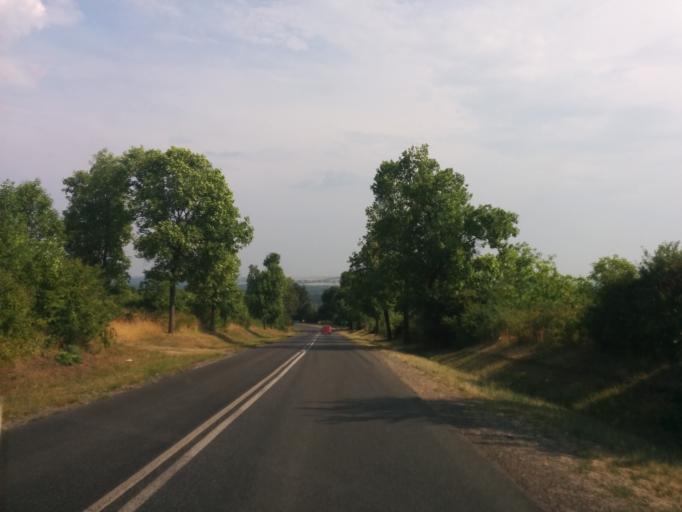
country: PL
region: Silesian Voivodeship
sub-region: Powiat myszkowski
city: Zarki
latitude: 50.6104
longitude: 19.3869
